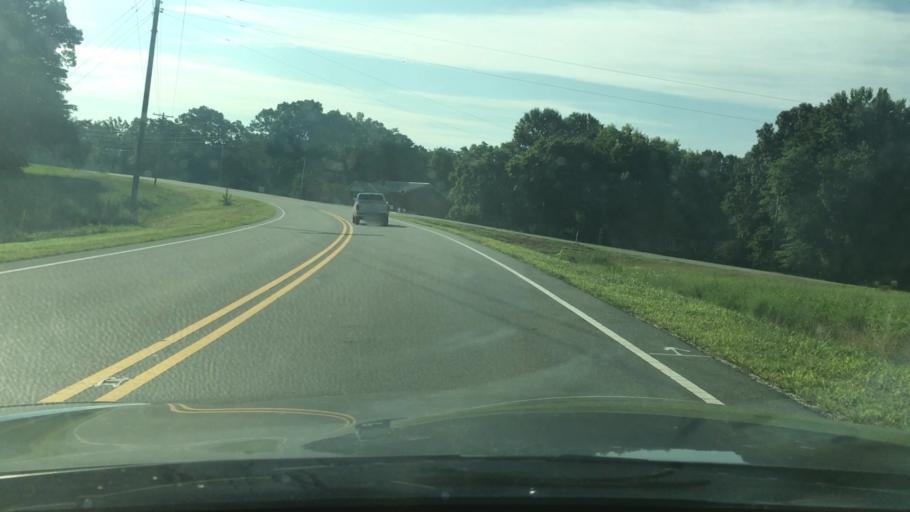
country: US
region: North Carolina
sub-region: Caswell County
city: Yanceyville
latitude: 36.2820
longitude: -79.3634
